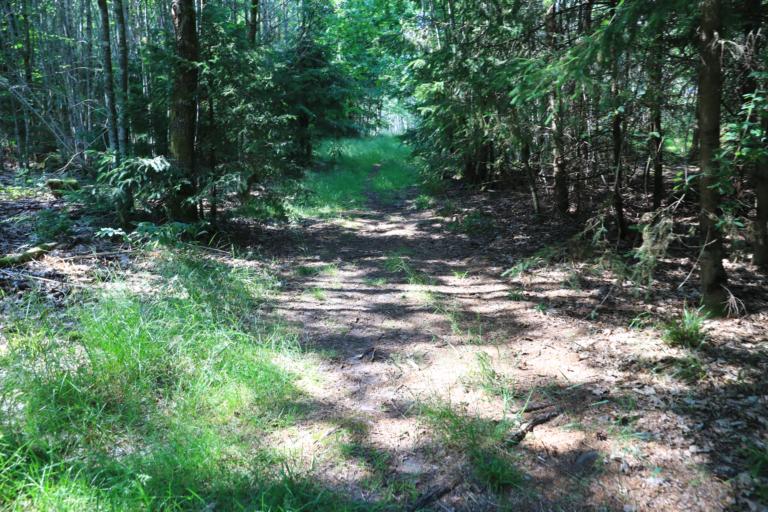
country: SE
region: Halland
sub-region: Varbergs Kommun
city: Varberg
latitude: 57.1706
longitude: 12.2938
